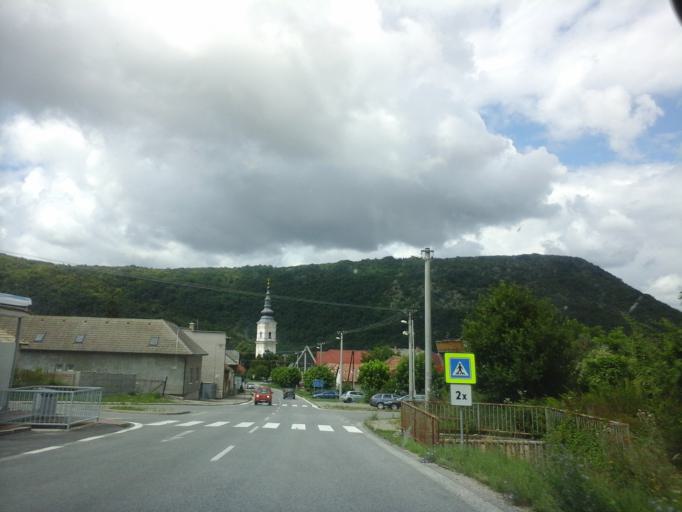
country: SK
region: Kosicky
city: Roznava
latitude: 48.5438
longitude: 20.4055
